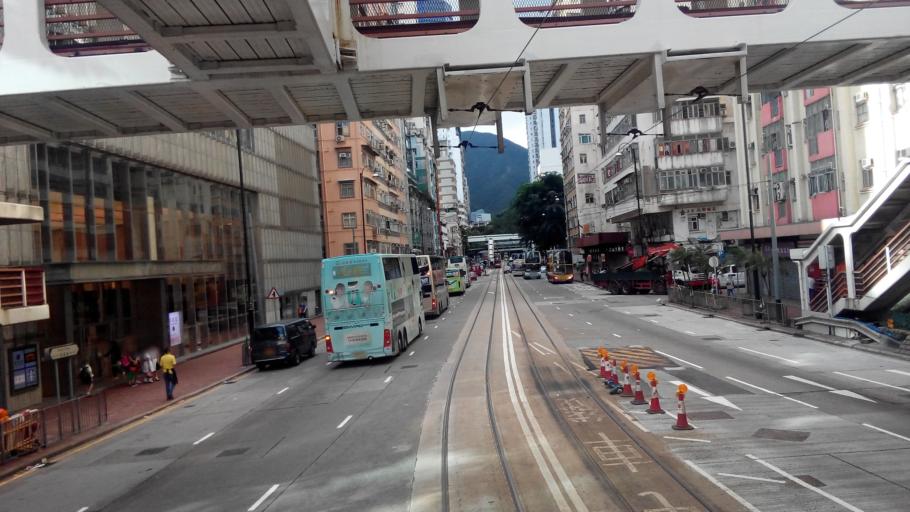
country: HK
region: Kowloon City
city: Kowloon
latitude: 22.2907
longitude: 114.2091
